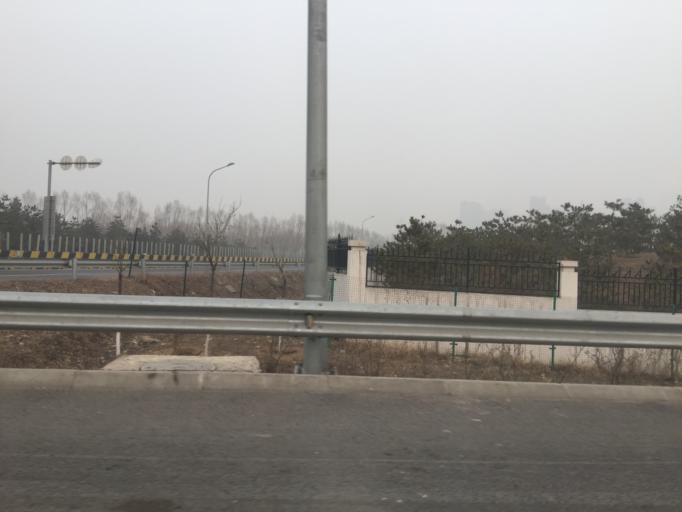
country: CN
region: Beijing
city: Qinghe
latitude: 40.0128
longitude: 116.3264
